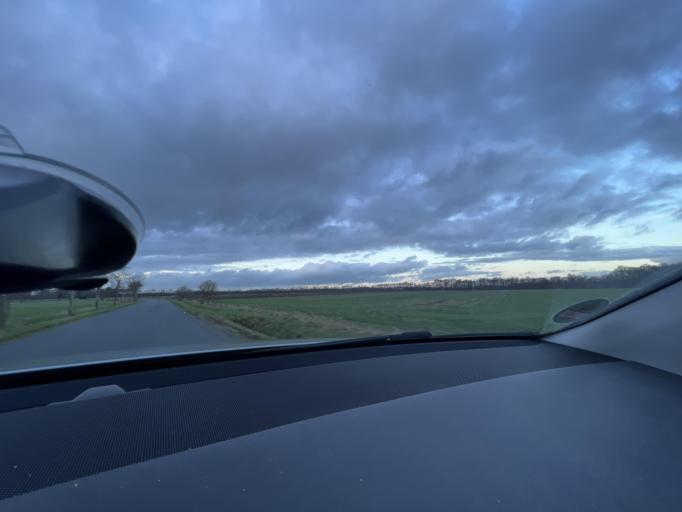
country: DE
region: Lower Saxony
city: Hatten
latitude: 53.0582
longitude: 8.3356
